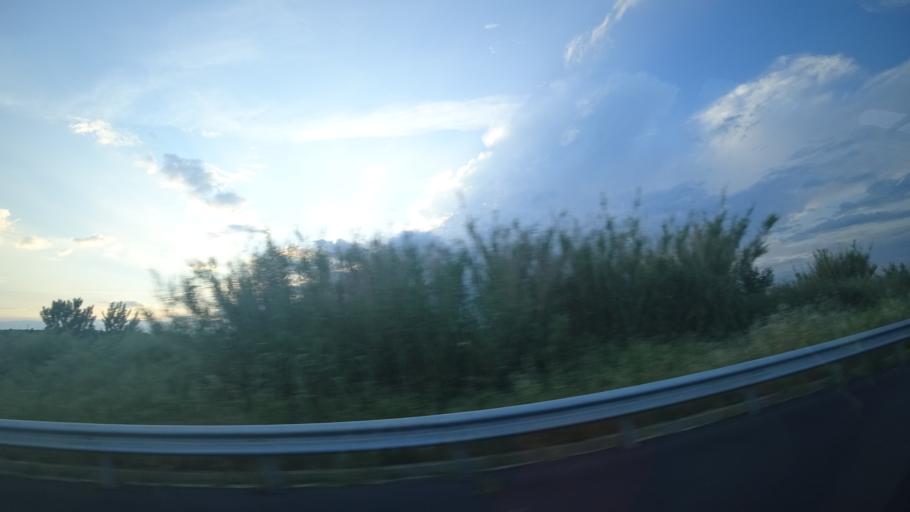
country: FR
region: Languedoc-Roussillon
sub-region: Departement de l'Herault
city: Lezignan-la-Cebe
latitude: 43.4896
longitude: 3.4438
